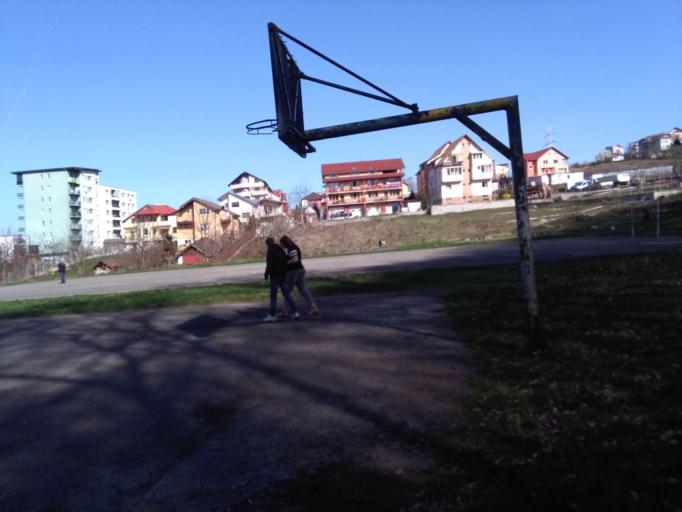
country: RO
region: Cluj
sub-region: Municipiul Cluj-Napoca
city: Cluj-Napoca
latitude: 46.7484
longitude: 23.5548
